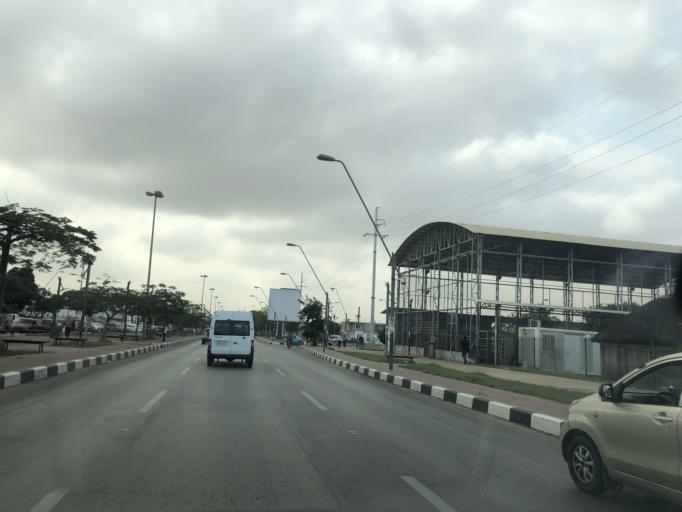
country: AO
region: Luanda
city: Luanda
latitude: -8.8298
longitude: 13.2482
